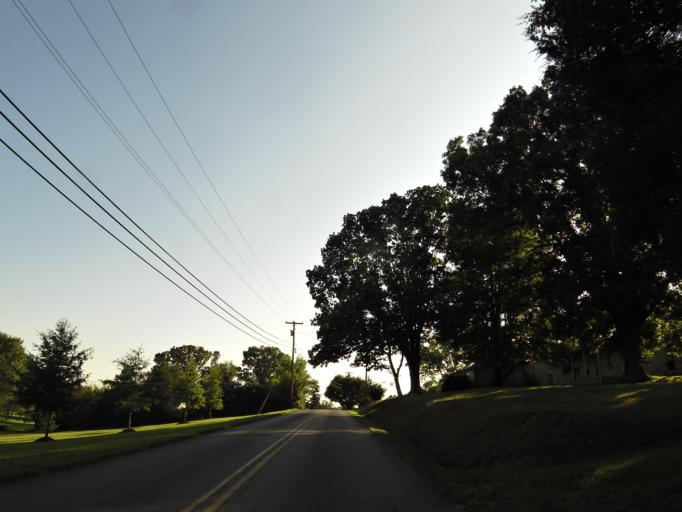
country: US
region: Tennessee
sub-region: Blount County
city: Maryville
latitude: 35.7192
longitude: -83.9150
